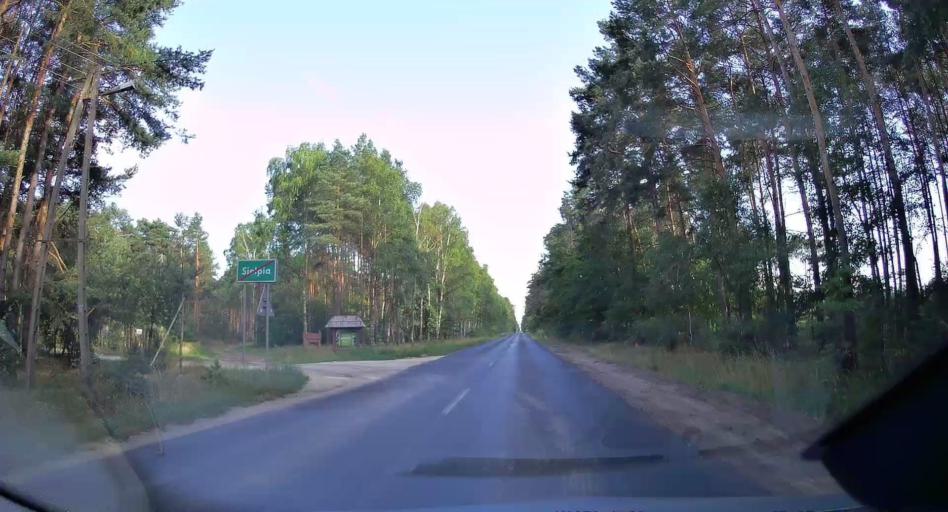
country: PL
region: Swietokrzyskie
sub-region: Powiat konecki
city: Smykow
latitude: 51.1085
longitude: 20.3499
